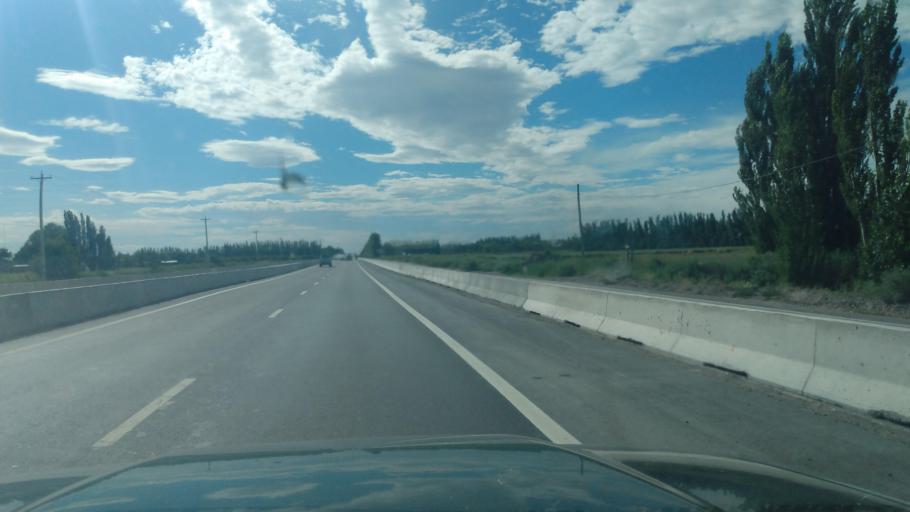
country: AR
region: Rio Negro
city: General Fernandez Oro
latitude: -38.9838
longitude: -67.9277
